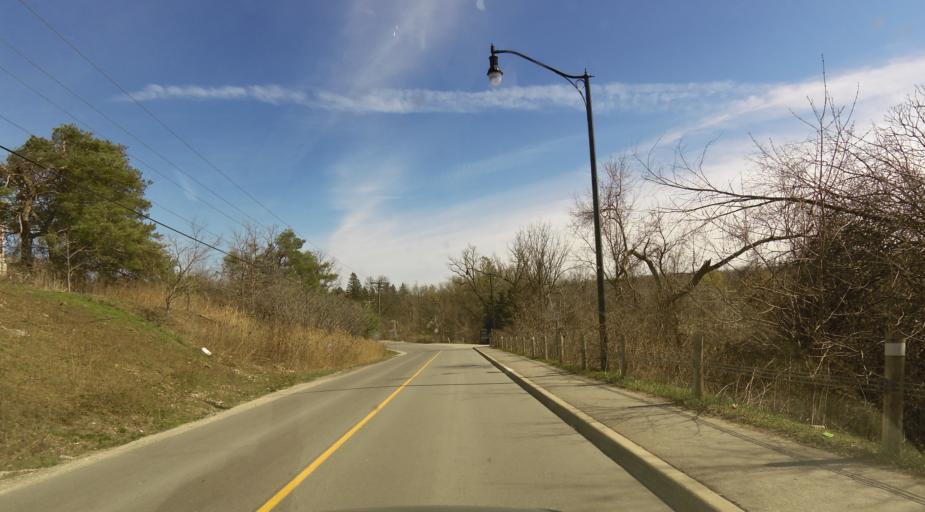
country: CA
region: Ontario
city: Brampton
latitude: 43.6481
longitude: -79.7804
